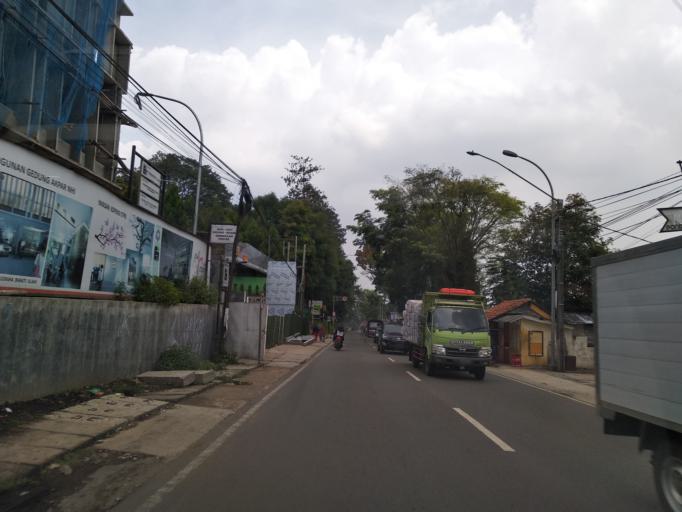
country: ID
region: West Java
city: Lembang
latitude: -6.8318
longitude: 107.6058
